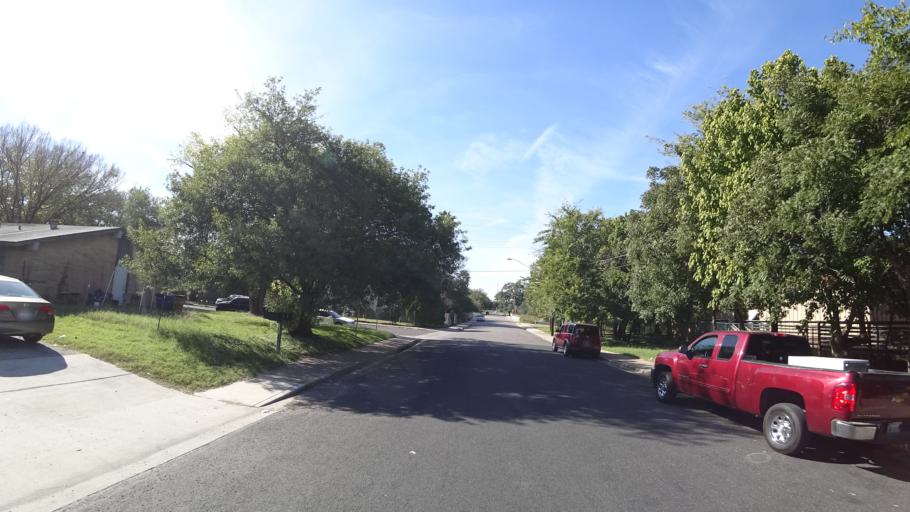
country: US
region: Texas
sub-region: Travis County
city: Austin
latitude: 30.2608
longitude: -97.6836
